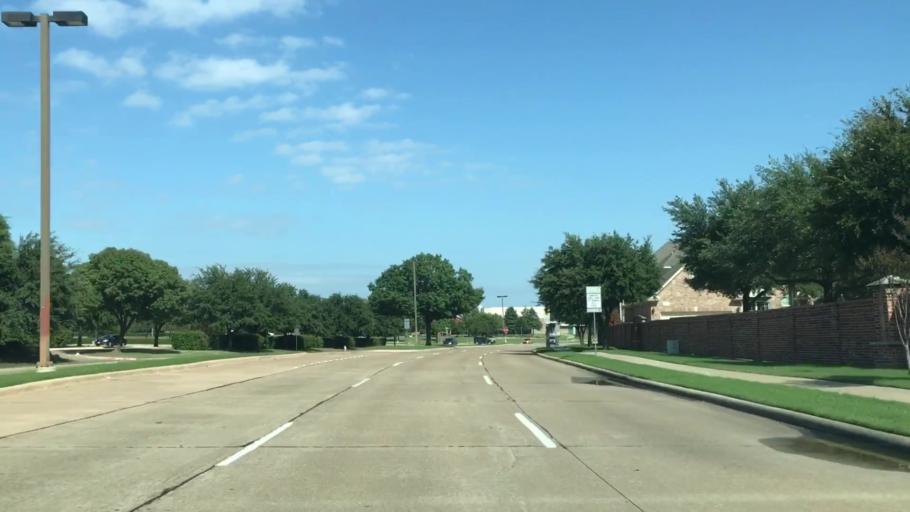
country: US
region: Texas
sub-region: Dallas County
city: Coppell
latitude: 32.9154
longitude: -96.9818
